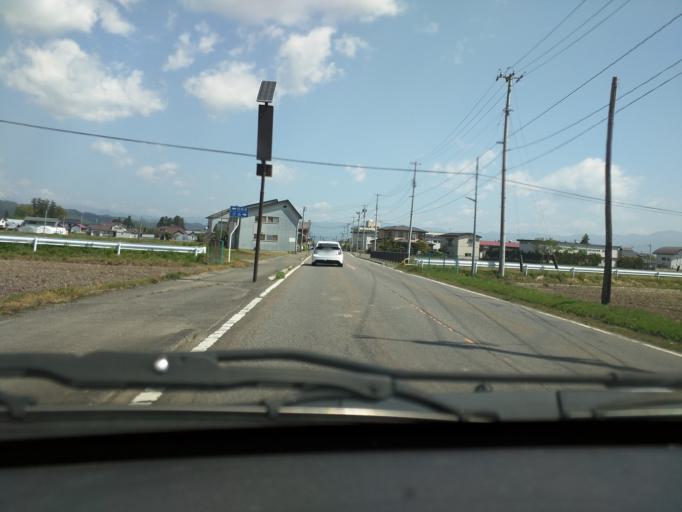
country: JP
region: Fukushima
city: Kitakata
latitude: 37.5849
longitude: 139.8348
